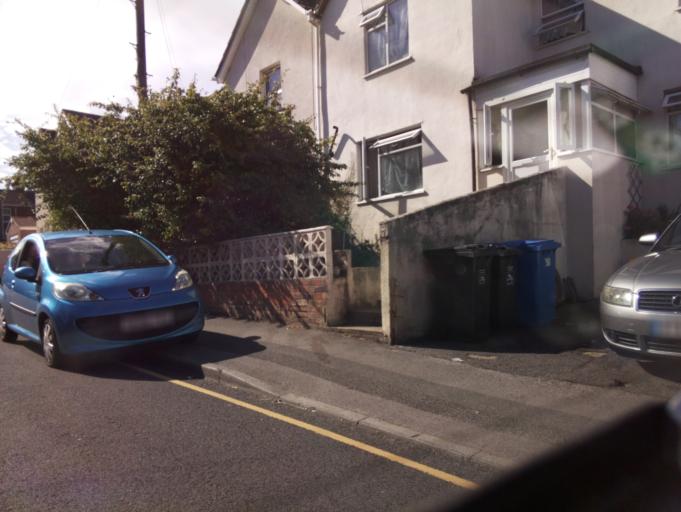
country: GB
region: England
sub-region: Dorset
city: Parkstone
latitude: 50.7274
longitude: -1.9412
